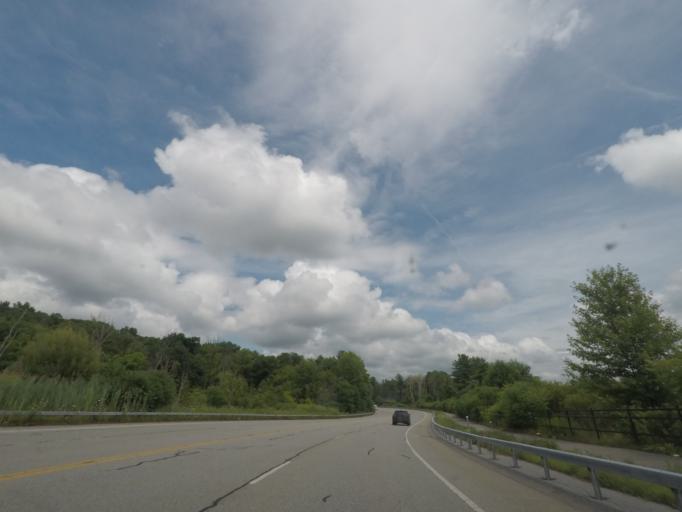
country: US
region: New York
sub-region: Saratoga County
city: Country Knolls
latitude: 42.9518
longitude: -73.7821
